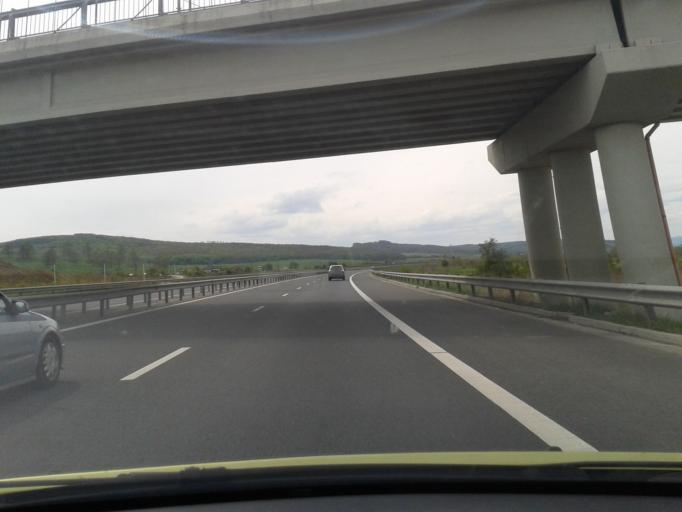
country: RO
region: Hunedoara
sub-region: Comuna Turdas
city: Turdas
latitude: 45.8407
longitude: 23.1222
